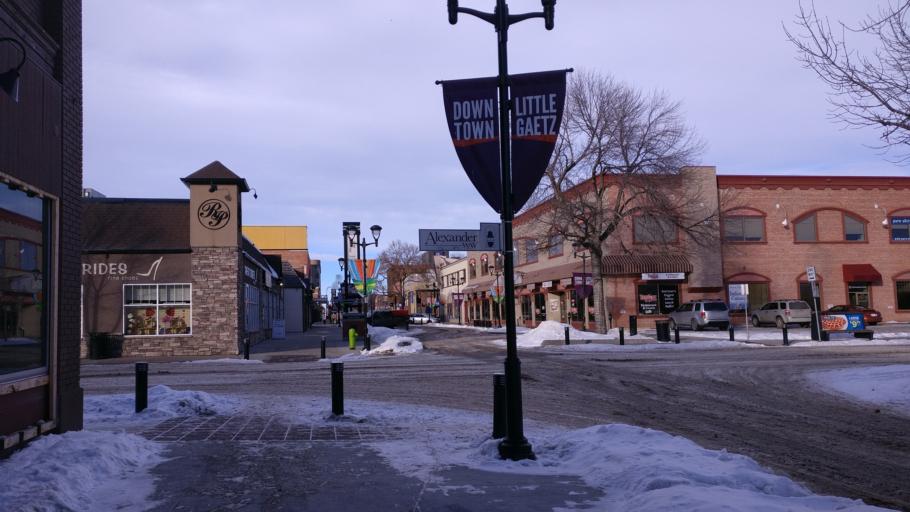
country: CA
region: Alberta
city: Red Deer
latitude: 52.2671
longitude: -113.8141
